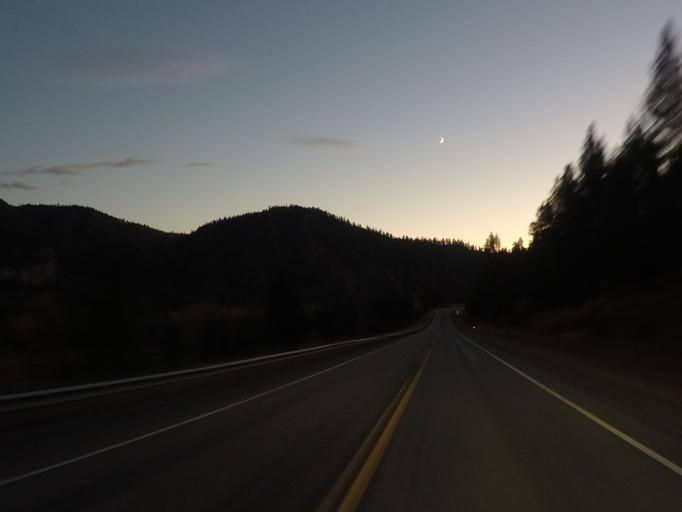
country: US
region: Montana
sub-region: Missoula County
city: Seeley Lake
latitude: 47.0265
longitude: -113.2871
